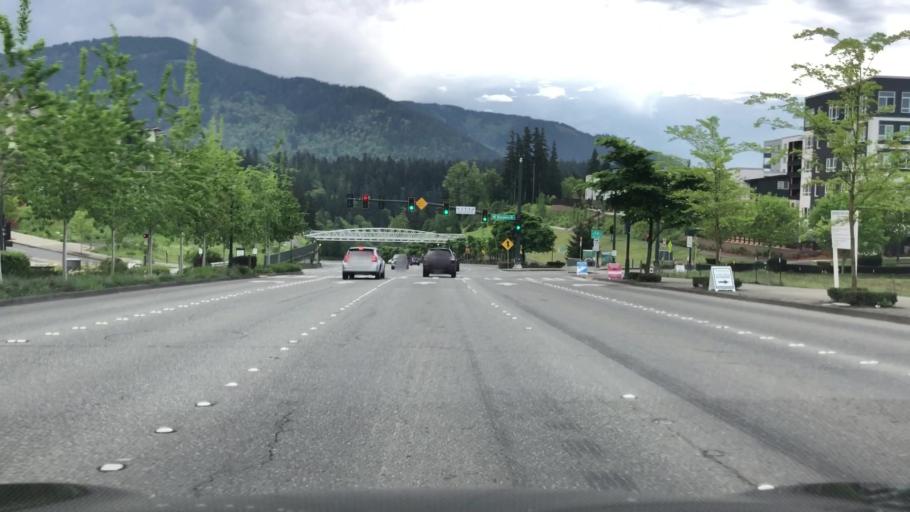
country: US
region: Washington
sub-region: King County
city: Issaquah
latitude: 47.5398
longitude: -122.0199
